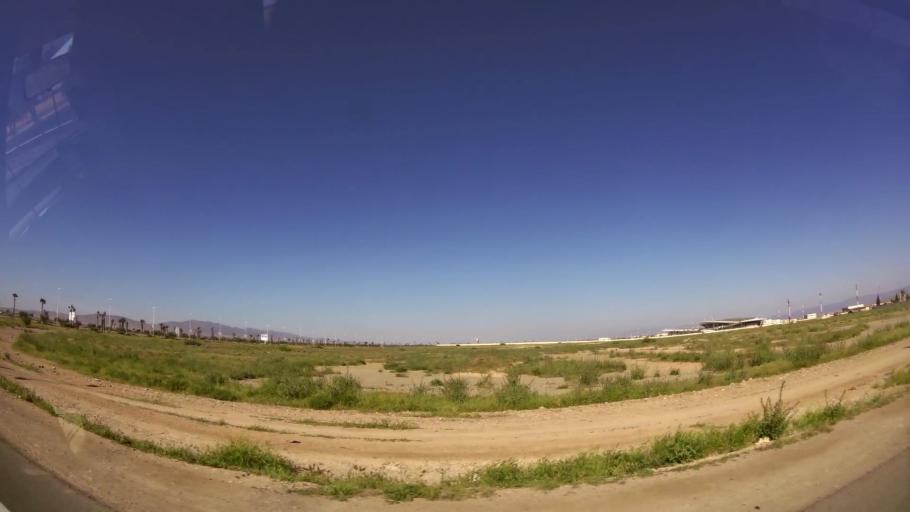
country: MA
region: Oriental
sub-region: Oujda-Angad
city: Oujda
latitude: 34.7886
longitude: -1.9506
